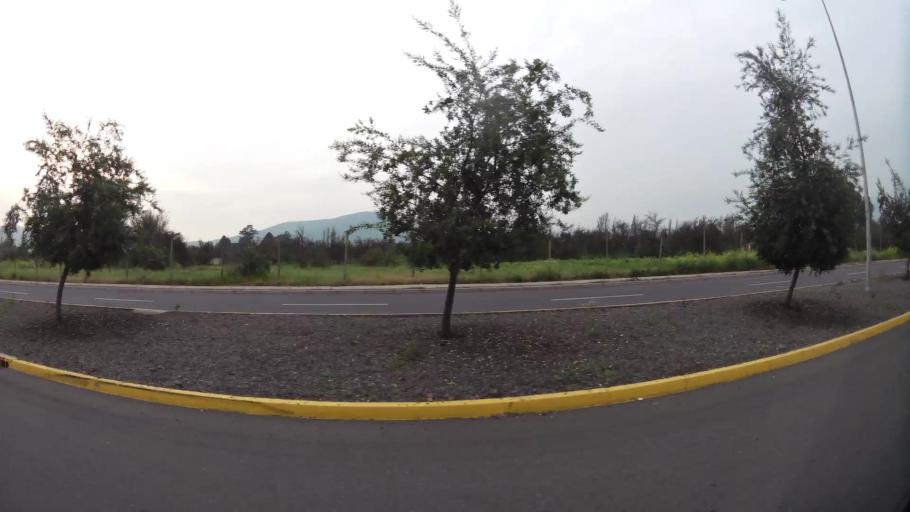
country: CL
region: Santiago Metropolitan
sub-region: Provincia de Chacabuco
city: Chicureo Abajo
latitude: -33.2648
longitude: -70.6228
